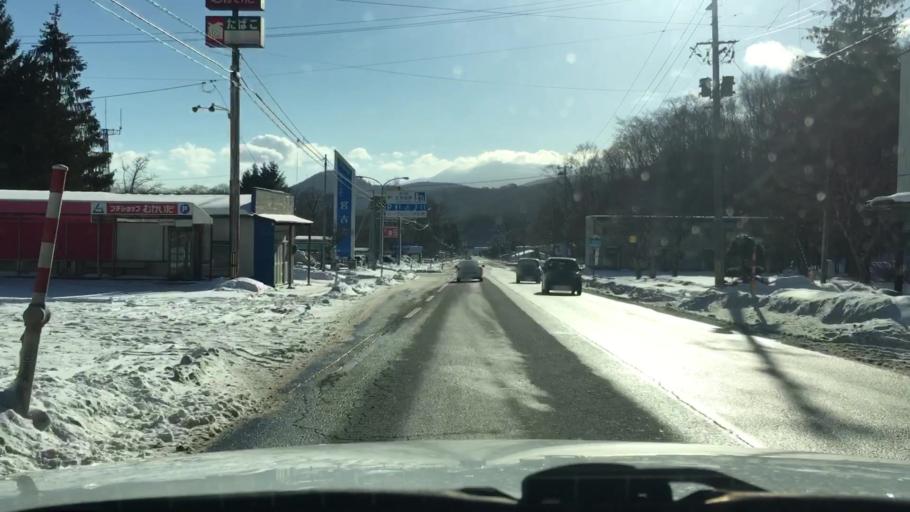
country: JP
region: Iwate
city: Morioka-shi
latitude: 39.6517
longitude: 141.3522
